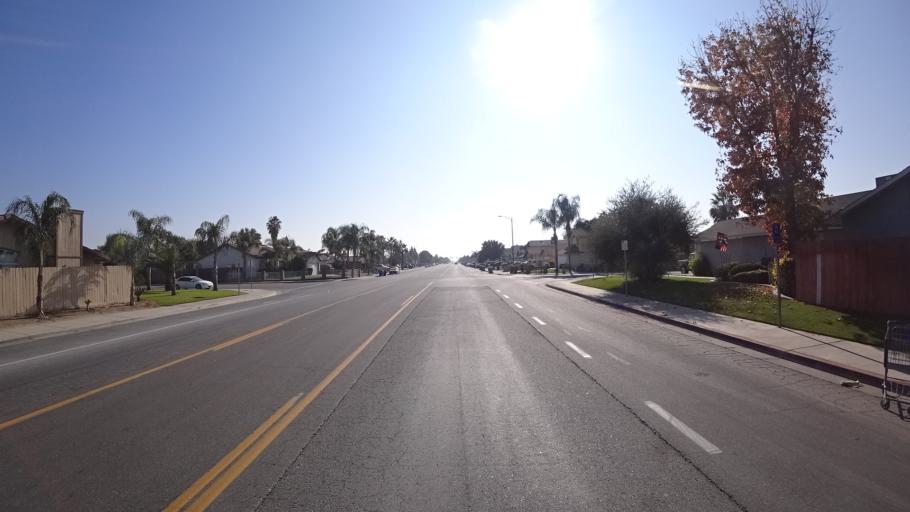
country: US
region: California
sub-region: Kern County
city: Greenfield
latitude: 35.2994
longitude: -119.0120
